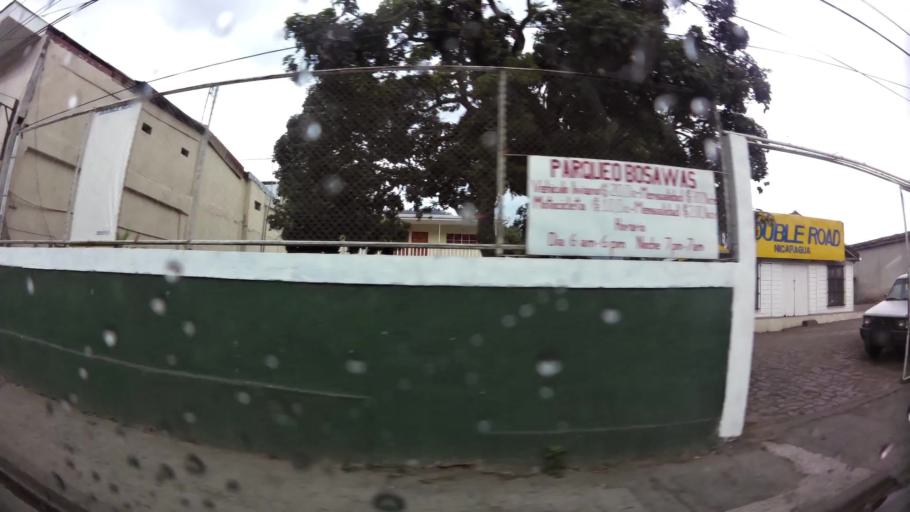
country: NI
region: Jinotega
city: Jinotega
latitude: 13.0948
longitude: -86.0026
